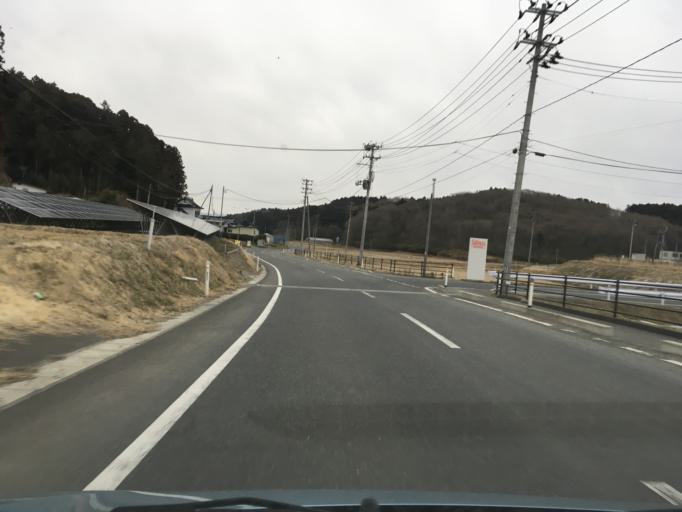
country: JP
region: Miyagi
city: Wakuya
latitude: 38.6996
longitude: 141.1728
